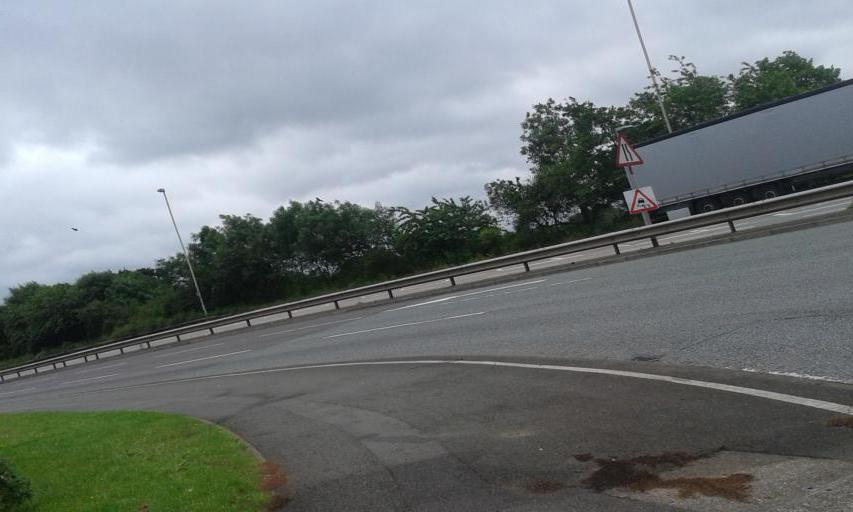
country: GB
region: England
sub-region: Leicestershire
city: Blaby
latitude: 52.5944
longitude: -1.1800
